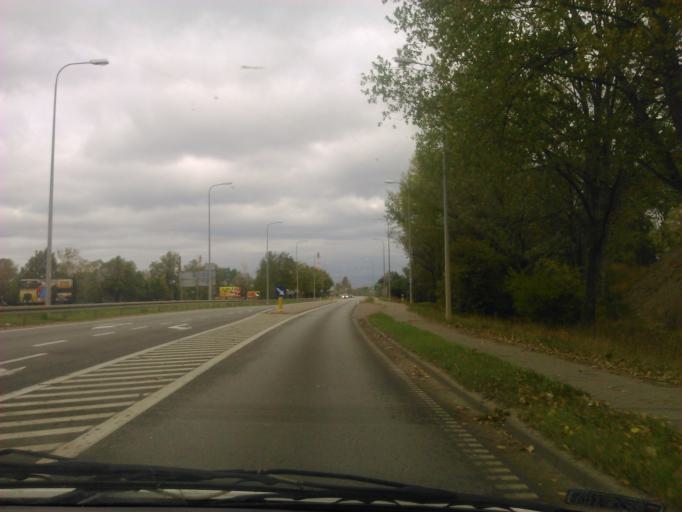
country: PL
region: Pomeranian Voivodeship
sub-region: Gdansk
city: Gdansk
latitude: 54.3279
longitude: 18.7445
